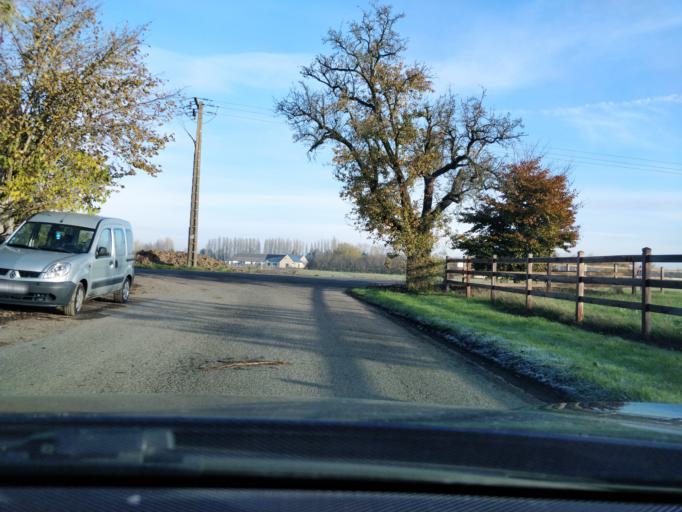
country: FR
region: Ile-de-France
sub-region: Departement de l'Essonne
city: Limours
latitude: 48.6520
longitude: 2.0923
